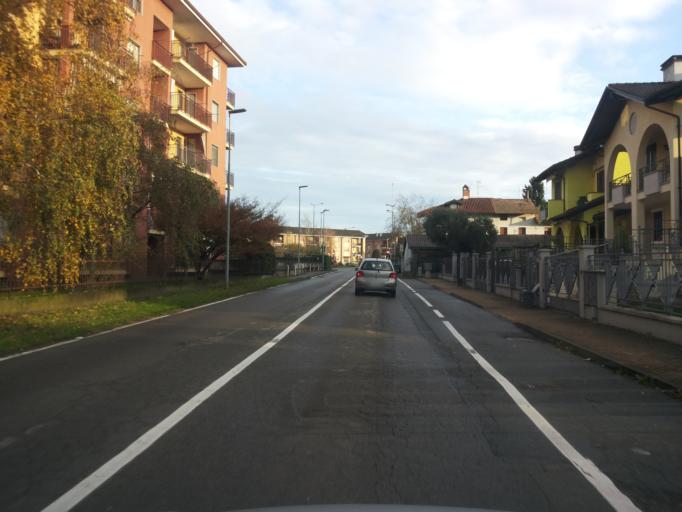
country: IT
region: Piedmont
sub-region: Provincia di Vercelli
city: Santhia
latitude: 45.3690
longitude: 8.1585
